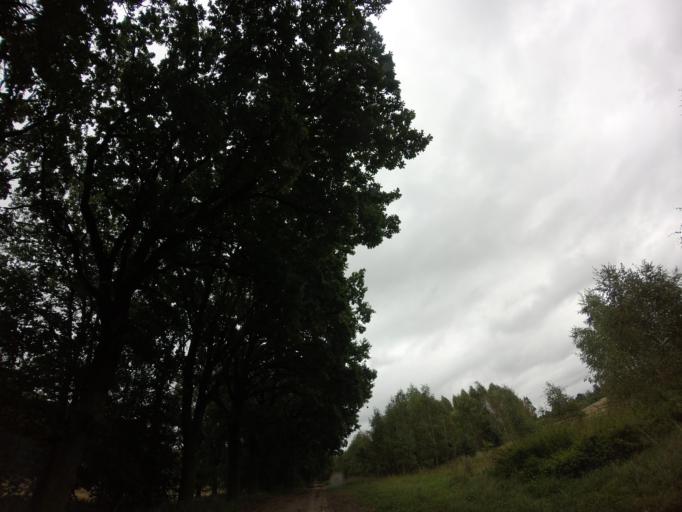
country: PL
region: West Pomeranian Voivodeship
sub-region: Powiat choszczenski
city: Choszczno
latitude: 53.1634
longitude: 15.3482
